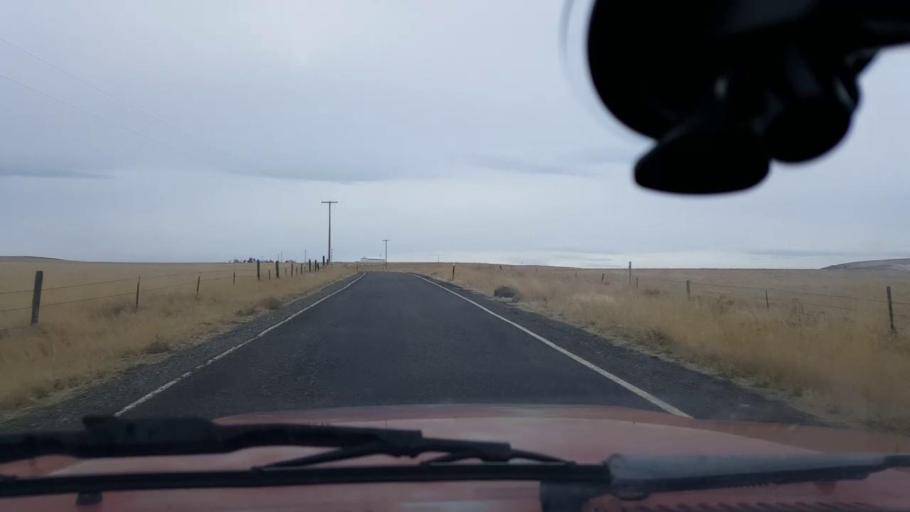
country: US
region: Washington
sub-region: Asotin County
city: Clarkston Heights-Vineland
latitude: 46.3280
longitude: -117.3233
